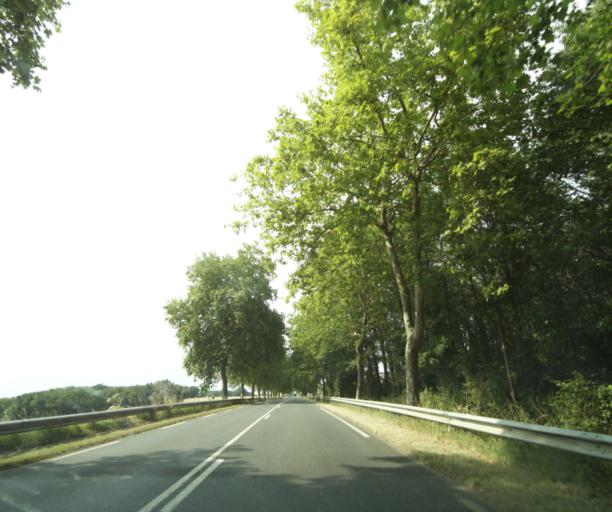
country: FR
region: Centre
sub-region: Departement d'Indre-et-Loire
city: Saint-Paterne-Racan
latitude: 47.6150
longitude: 0.5071
